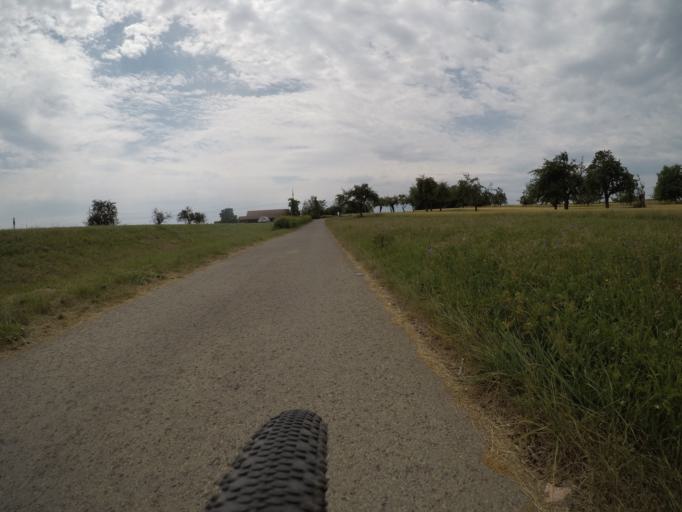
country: DE
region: Baden-Wuerttemberg
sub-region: Regierungsbezirk Stuttgart
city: Magstadt
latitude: 48.7182
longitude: 8.9547
